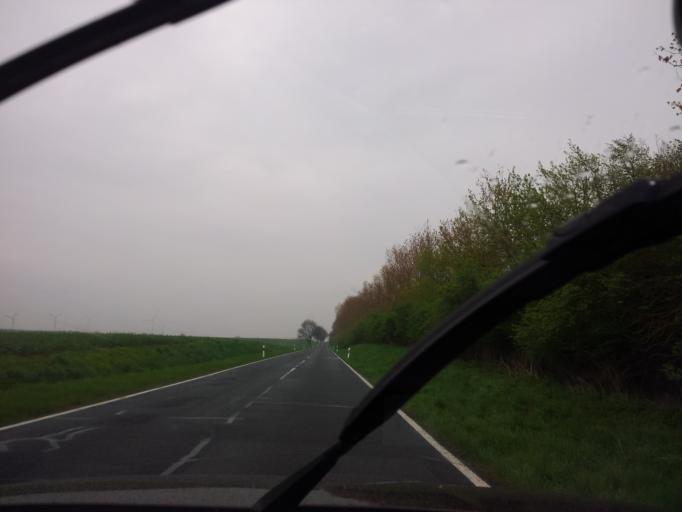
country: DE
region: Brandenburg
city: Treuenbrietzen
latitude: 51.9906
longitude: 12.8712
